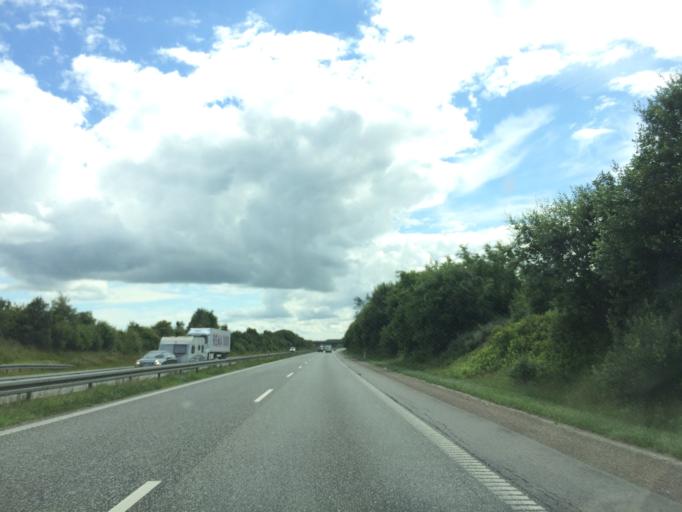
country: DK
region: North Denmark
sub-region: Mariagerfjord Kommune
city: Hobro
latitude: 56.6584
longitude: 9.7361
